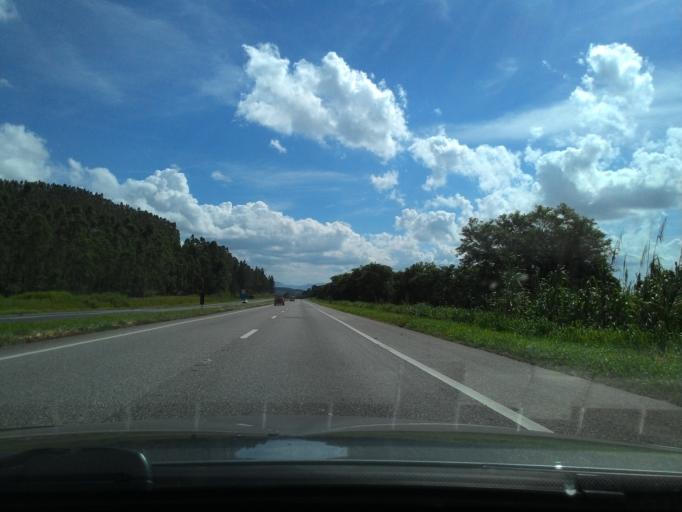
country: BR
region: Sao Paulo
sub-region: Jacupiranga
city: Jacupiranga
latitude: -24.7139
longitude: -48.0294
